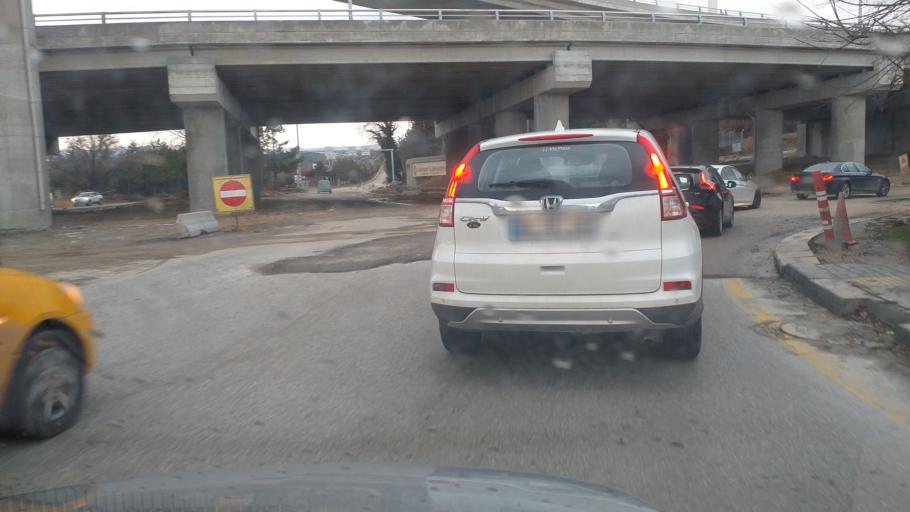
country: TR
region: Ankara
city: Batikent
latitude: 39.8971
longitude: 32.7335
